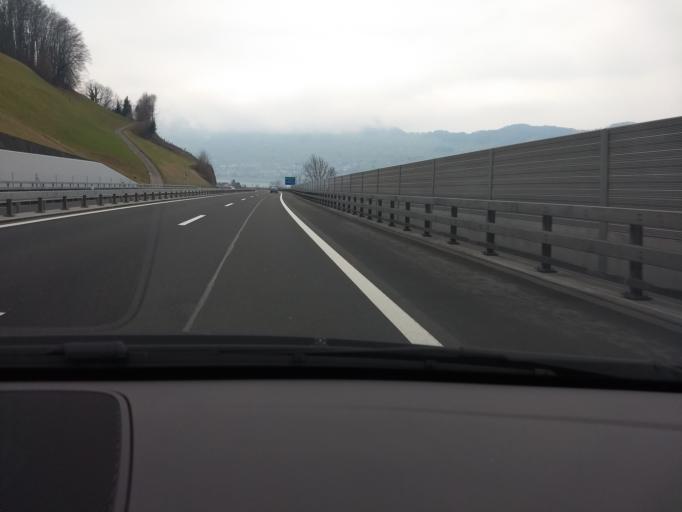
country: CH
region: Nidwalden
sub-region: Nidwalden
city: Beckenried
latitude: 46.9691
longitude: 8.4548
